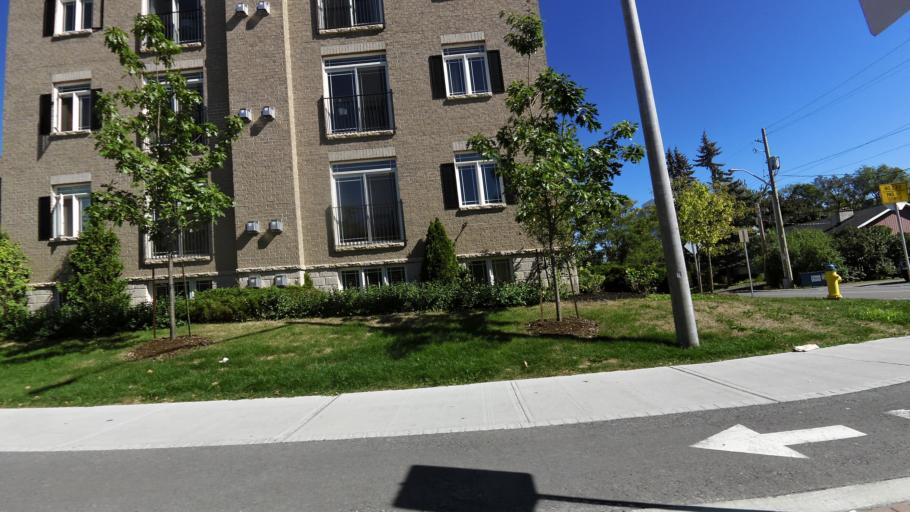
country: CA
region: Ontario
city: Ottawa
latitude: 45.3817
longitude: -75.7475
